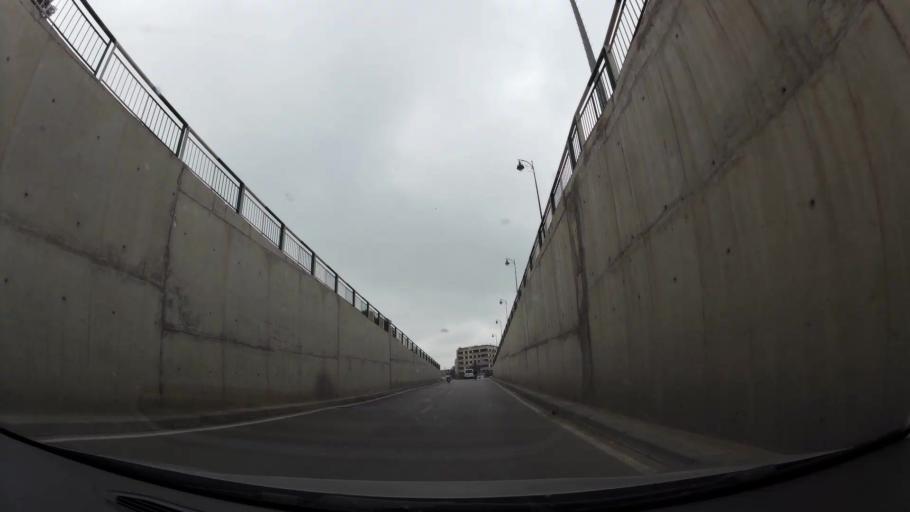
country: MA
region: Fes-Boulemane
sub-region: Fes
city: Fes
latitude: 34.0486
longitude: -5.0017
